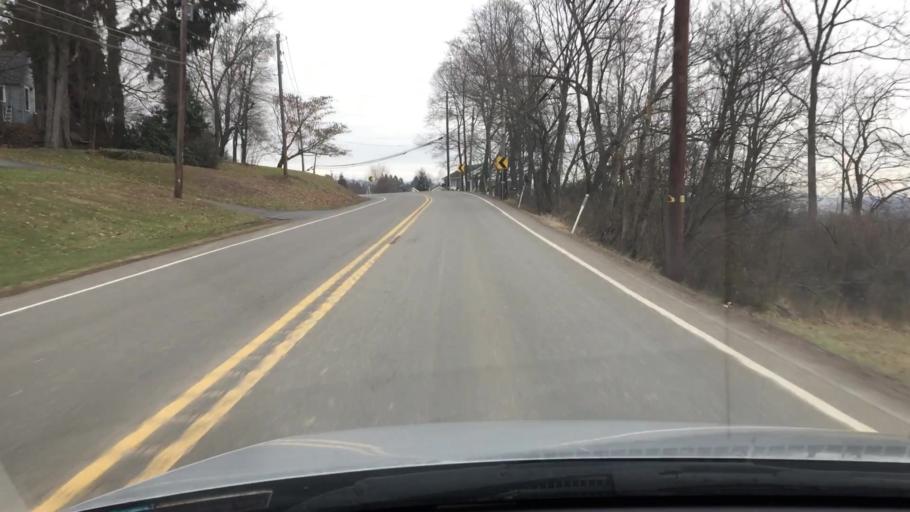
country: US
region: Pennsylvania
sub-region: Columbia County
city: Bloomsburg
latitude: 41.0162
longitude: -76.4386
